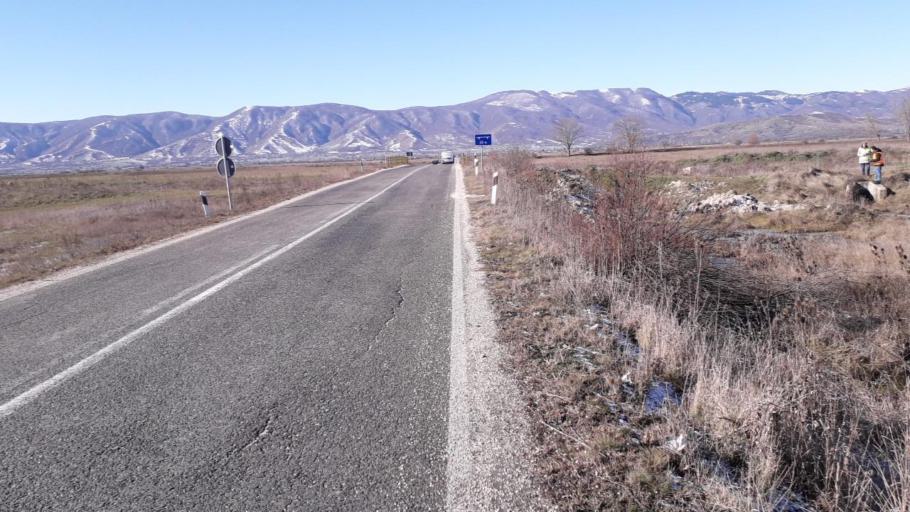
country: MK
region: Krivogastani
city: Krivogashtani
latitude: 41.3366
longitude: 21.3743
